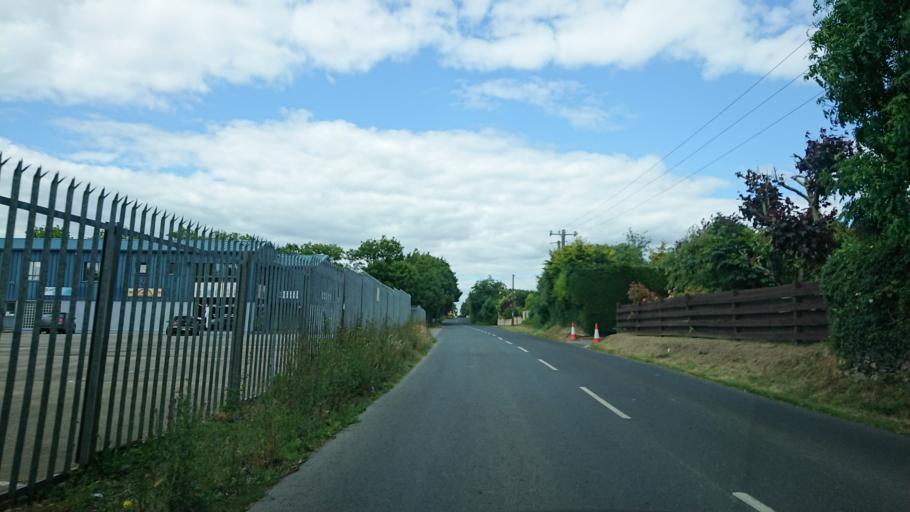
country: IE
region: Munster
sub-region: Waterford
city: Waterford
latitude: 52.2288
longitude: -7.1455
